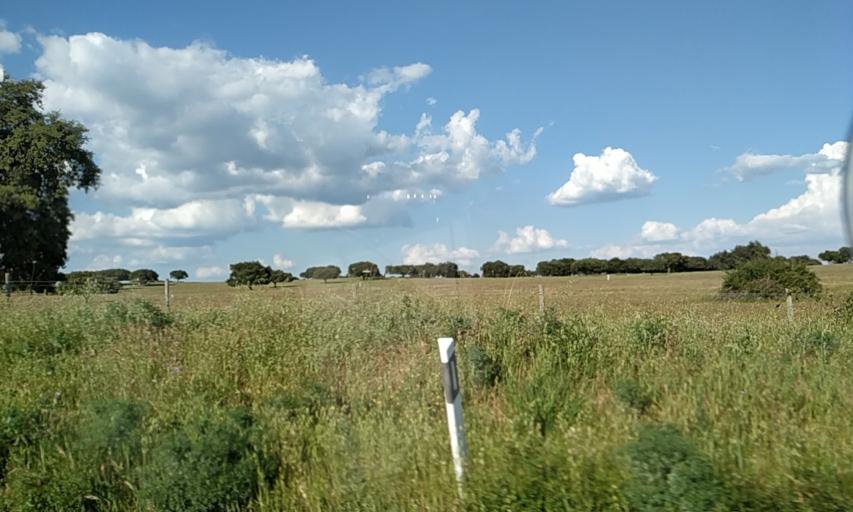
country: PT
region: Portalegre
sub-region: Portalegre
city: Urra
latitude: 39.1478
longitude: -7.4530
